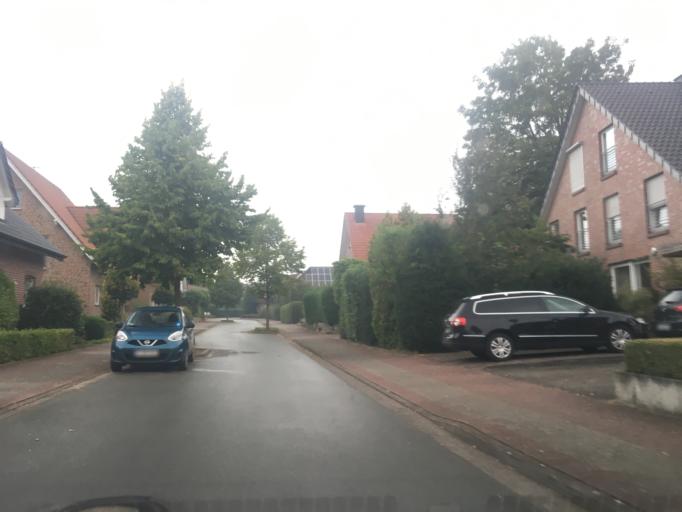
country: DE
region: North Rhine-Westphalia
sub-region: Regierungsbezirk Munster
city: Altenberge
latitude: 52.0398
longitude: 7.4686
